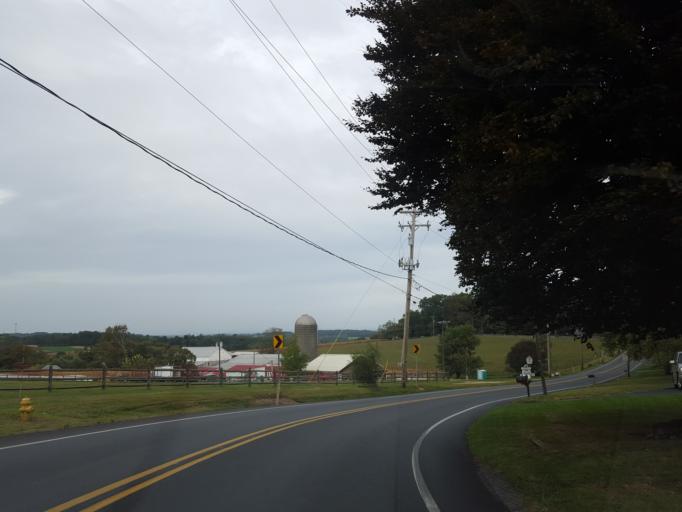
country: US
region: Pennsylvania
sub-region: York County
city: Jacobus
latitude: 39.9108
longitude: -76.7185
